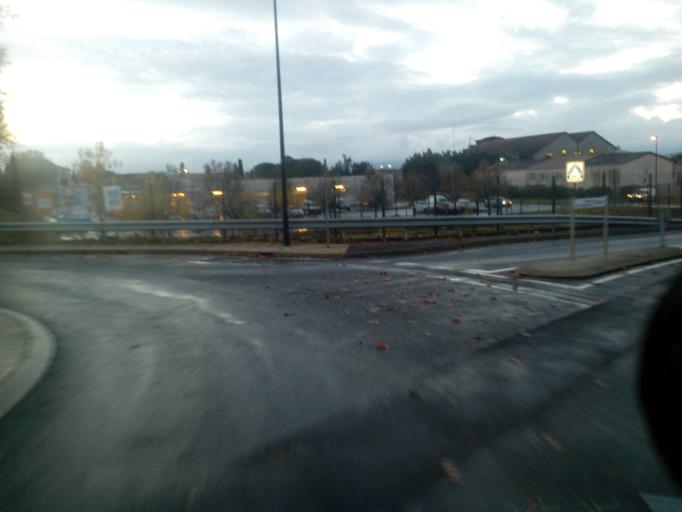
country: FR
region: Languedoc-Roussillon
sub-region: Departement de l'Herault
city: Gignac
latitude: 43.6559
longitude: 3.5555
